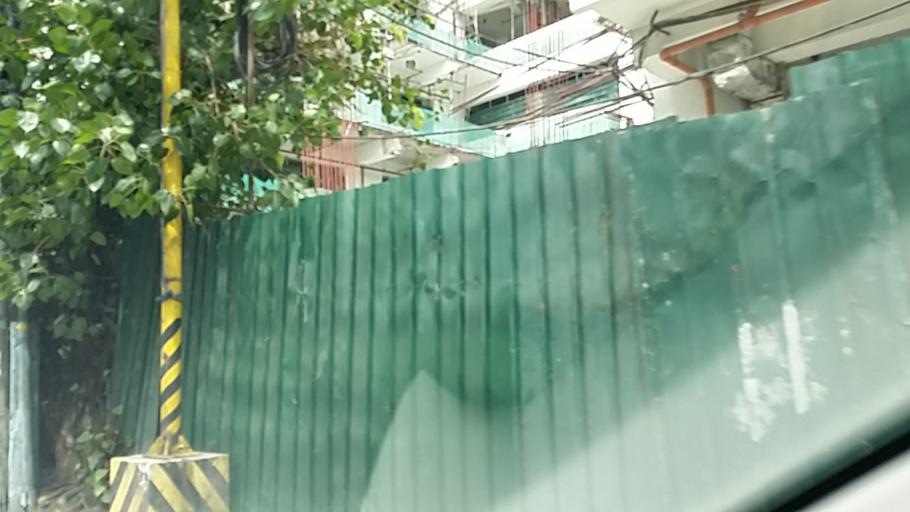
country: PH
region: Metro Manila
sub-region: Mandaluyong
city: Mandaluyong City
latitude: 14.5835
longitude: 121.0493
